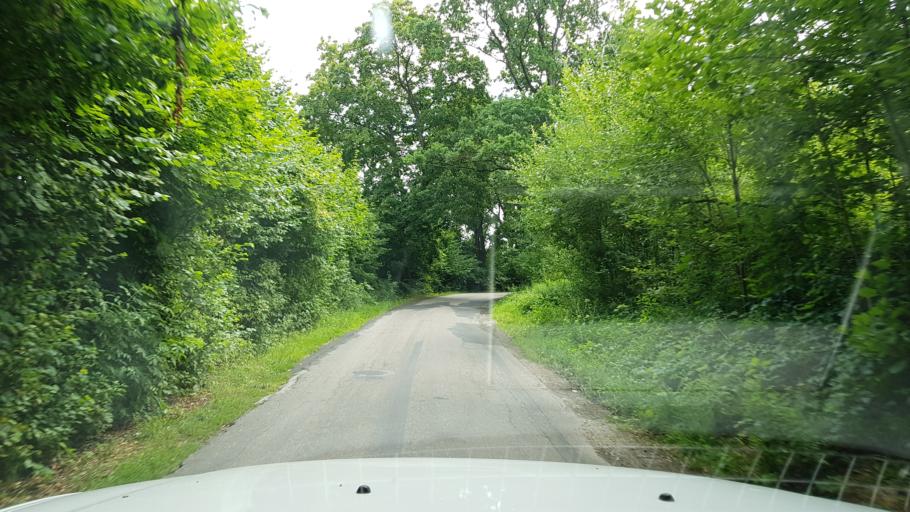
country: PL
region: West Pomeranian Voivodeship
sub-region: Powiat koszalinski
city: Mielno
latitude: 54.1588
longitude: 16.0749
